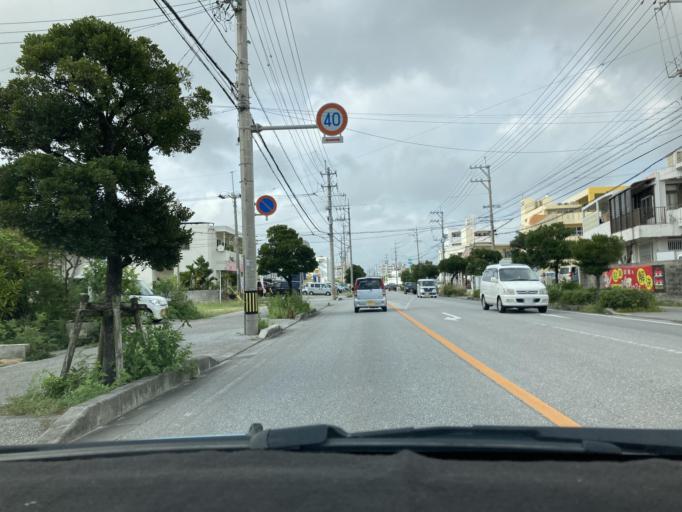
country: JP
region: Okinawa
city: Itoman
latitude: 26.1553
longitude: 127.6711
